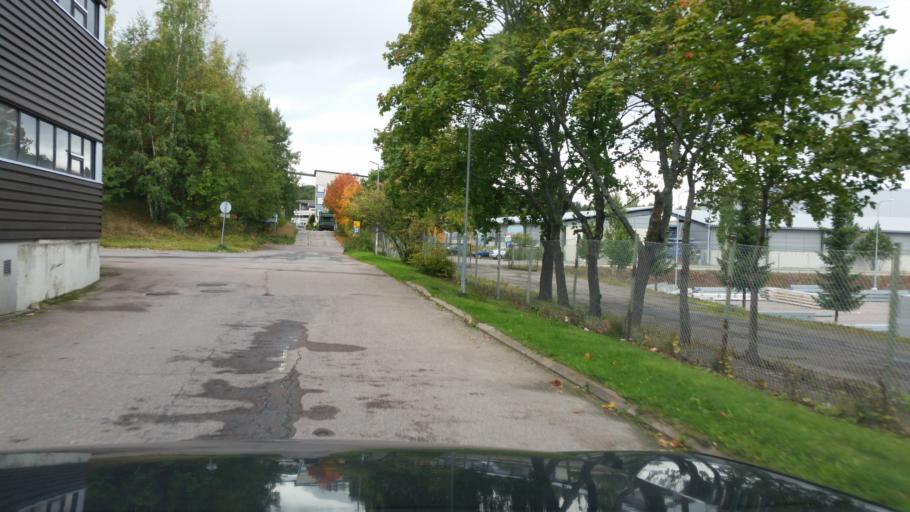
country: FI
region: Uusimaa
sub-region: Helsinki
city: Helsinki
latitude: 60.2348
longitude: 24.9760
